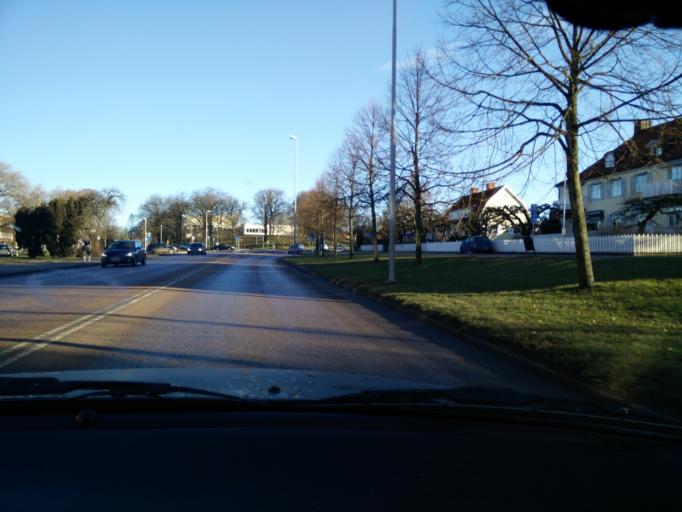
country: SE
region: Vaestmanland
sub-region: Vasteras
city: Vasteras
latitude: 59.6183
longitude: 16.5450
